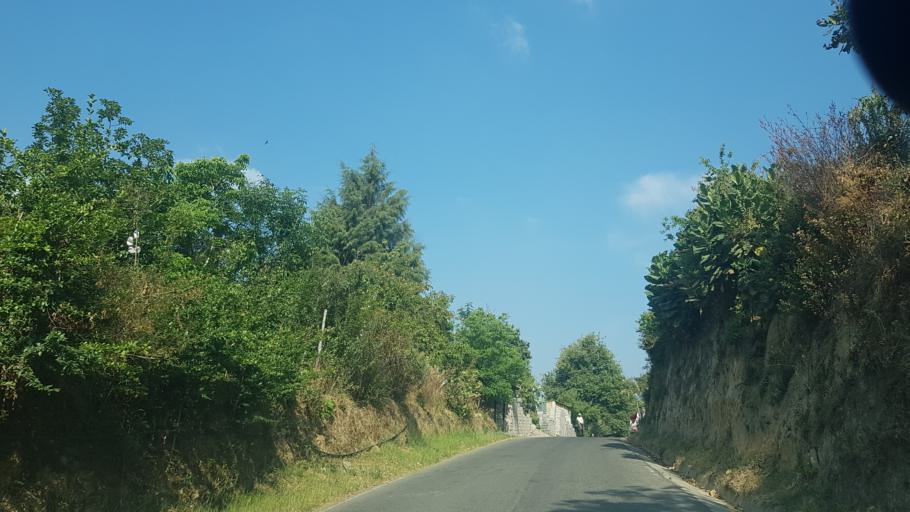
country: MX
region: Puebla
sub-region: Tochimilco
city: Santa Cruz Cuautomatitla
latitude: 18.8946
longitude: -98.6730
